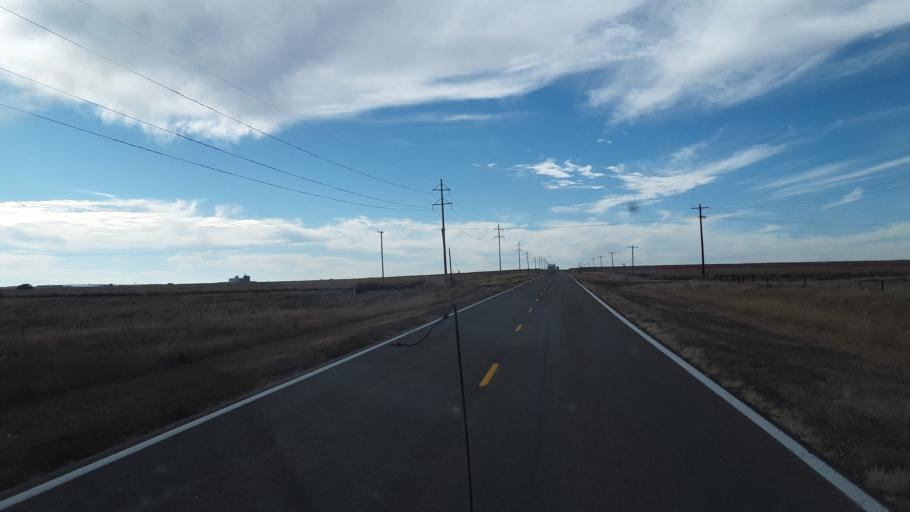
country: US
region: Kansas
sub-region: Hodgeman County
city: Jetmore
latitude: 38.0879
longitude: -99.8607
